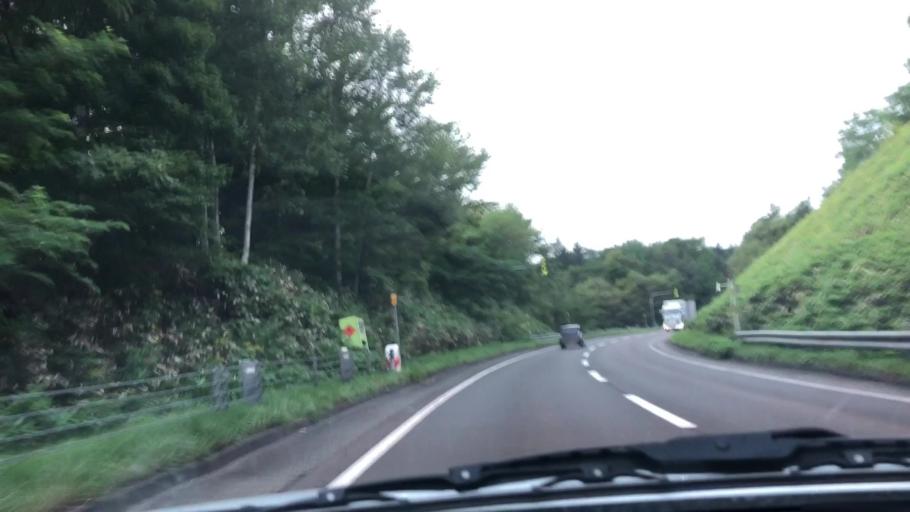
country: JP
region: Hokkaido
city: Iwamizawa
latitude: 42.9052
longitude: 142.1268
